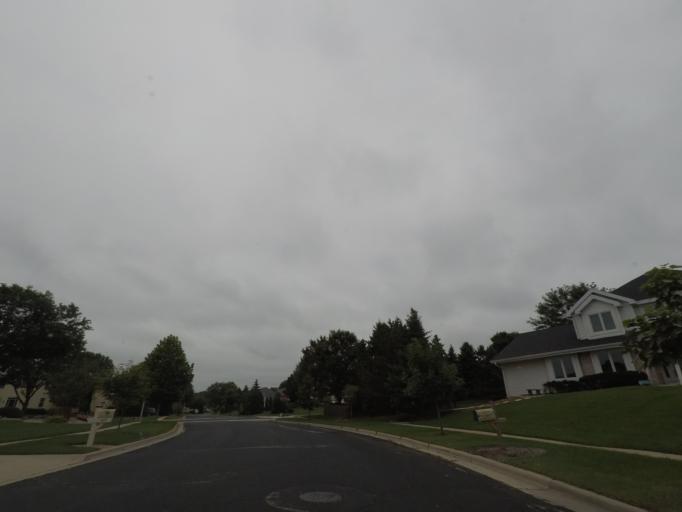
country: US
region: Wisconsin
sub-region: Dane County
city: Middleton
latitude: 43.0847
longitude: -89.4992
